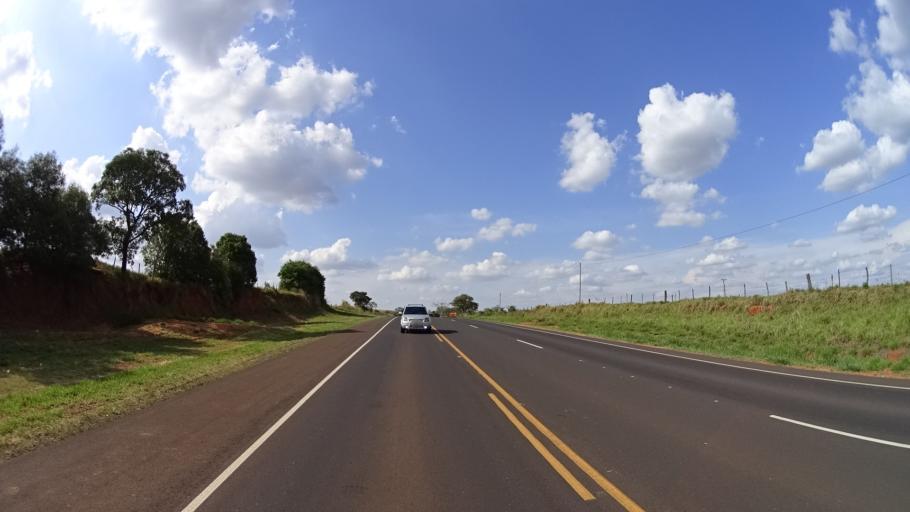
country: BR
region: Sao Paulo
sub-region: Urupes
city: Urupes
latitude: -21.0537
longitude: -49.2485
